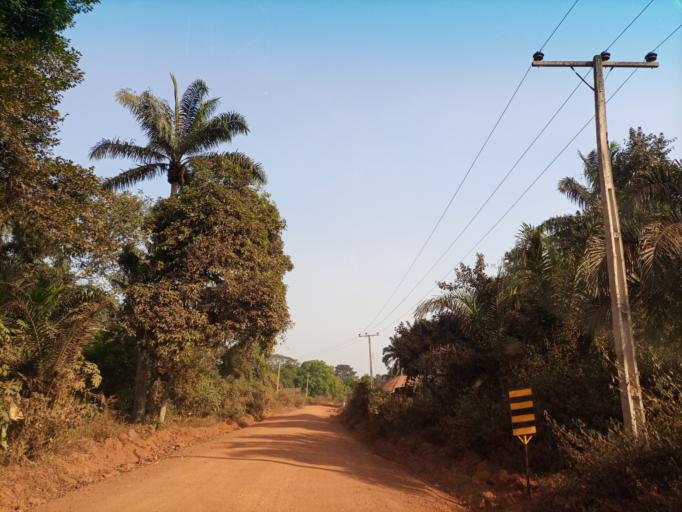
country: NG
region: Enugu
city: Opi
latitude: 6.7596
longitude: 7.4005
